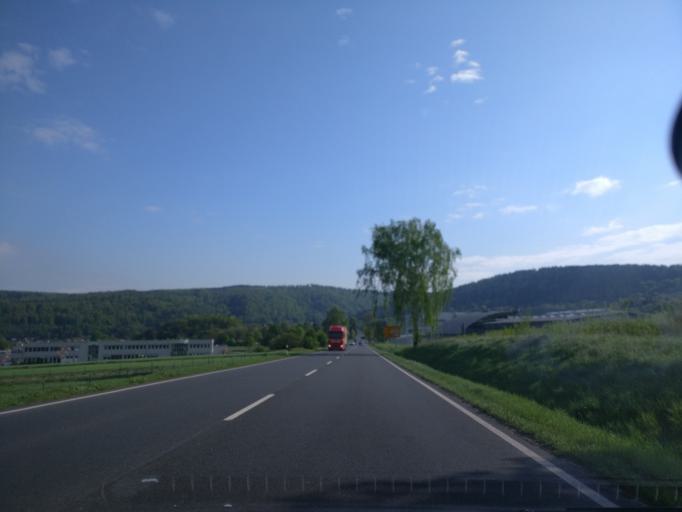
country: DE
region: Lower Saxony
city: Hannoversch Munden
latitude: 51.4351
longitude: 9.6536
